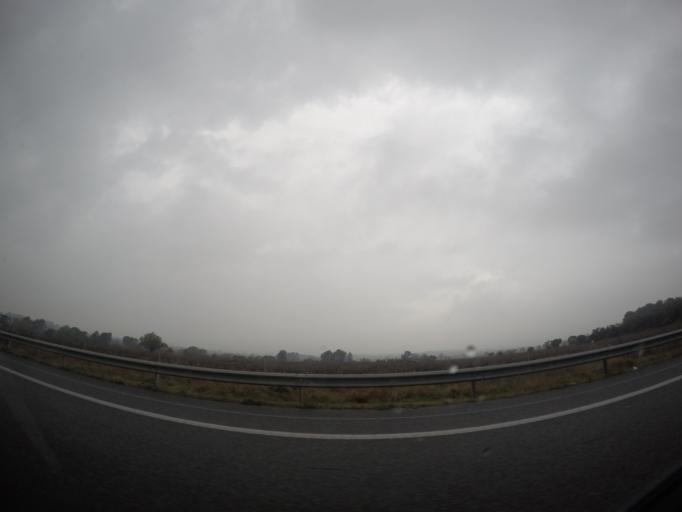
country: ES
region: Catalonia
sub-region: Provincia de Barcelona
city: Vilobi del Penedes
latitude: 41.3255
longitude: 1.6466
